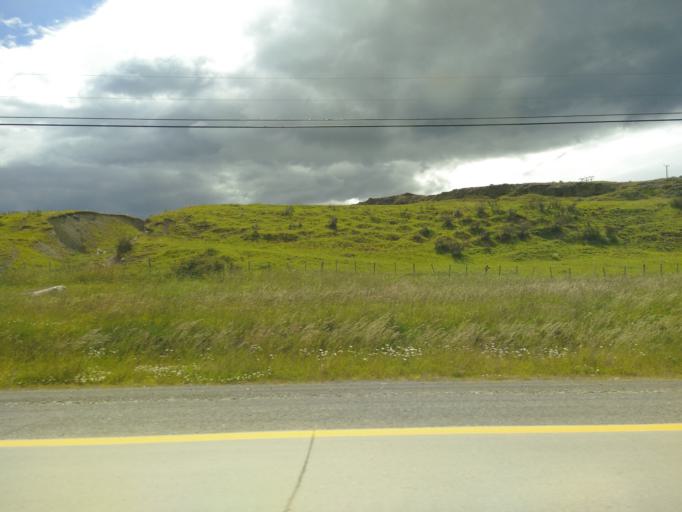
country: CL
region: Magallanes
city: Puerto Natales
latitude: -51.6980
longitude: -72.5233
